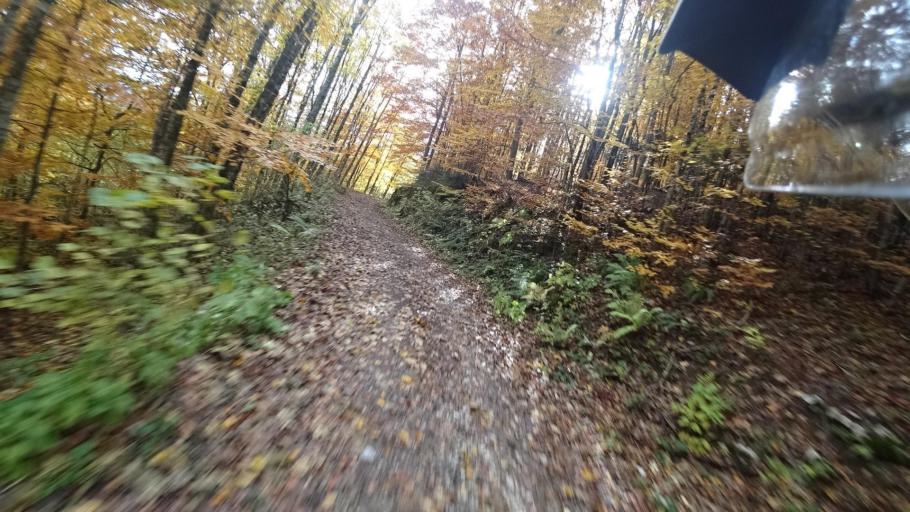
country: HR
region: Karlovacka
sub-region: Grad Ogulin
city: Ogulin
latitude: 45.1913
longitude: 15.1068
